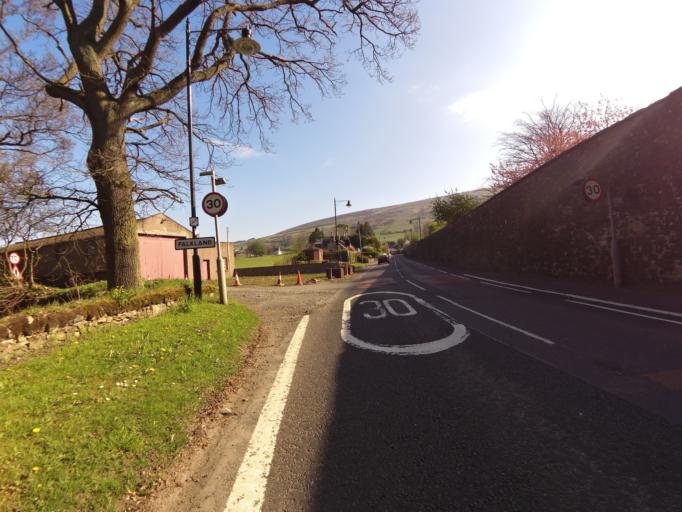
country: GB
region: Scotland
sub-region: Fife
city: Falkland
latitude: 56.2553
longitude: -3.2049
